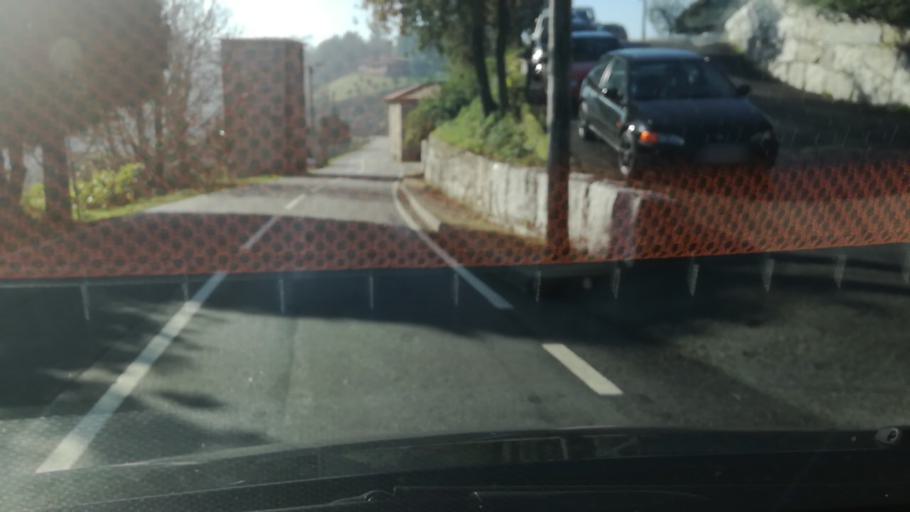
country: PT
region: Braga
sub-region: Guimaraes
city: Ponte
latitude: 41.5258
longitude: -8.3410
